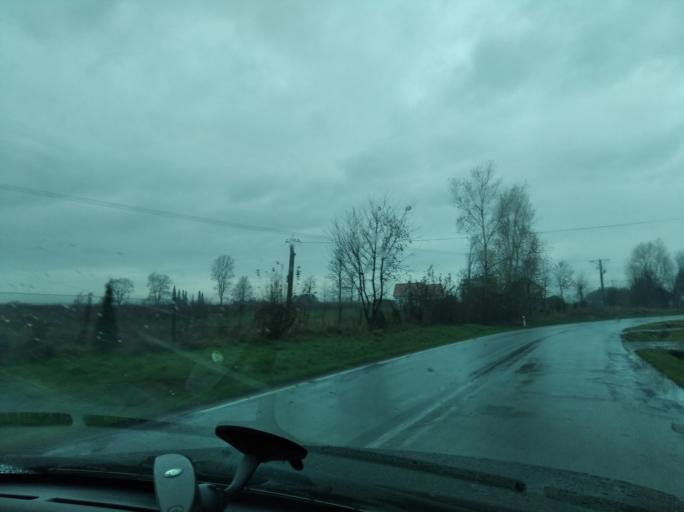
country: PL
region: Subcarpathian Voivodeship
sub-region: Powiat lancucki
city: Albigowa
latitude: 50.0333
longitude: 22.2284
